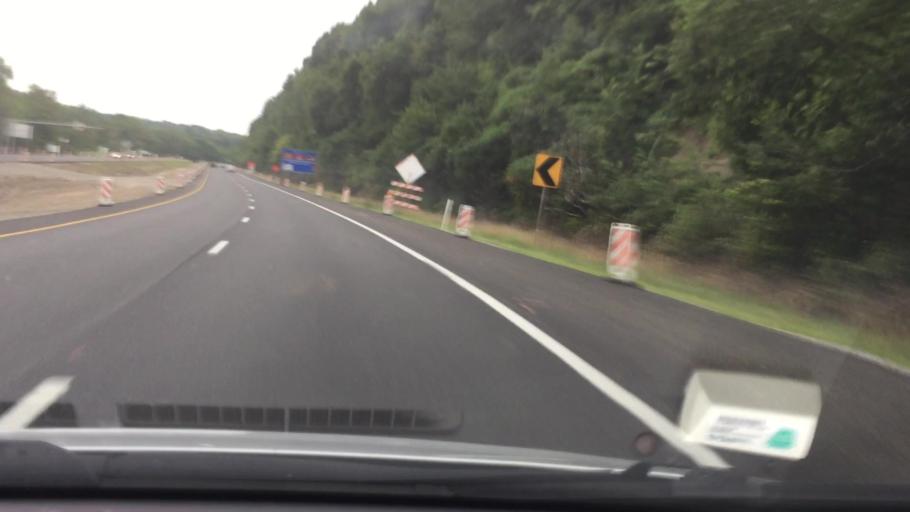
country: US
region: Pennsylvania
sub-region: Armstrong County
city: Freeport
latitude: 40.6521
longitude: -79.7247
